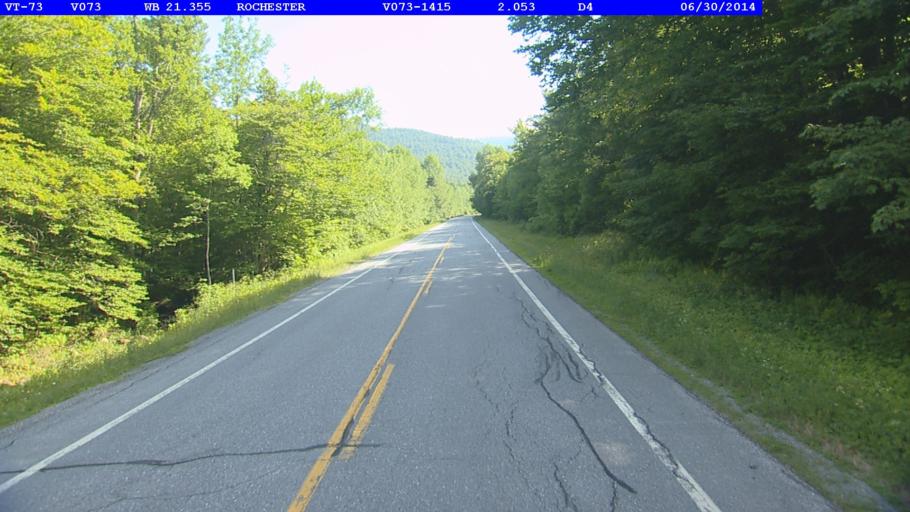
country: US
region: Vermont
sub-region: Rutland County
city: Brandon
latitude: 43.8483
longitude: -72.9274
